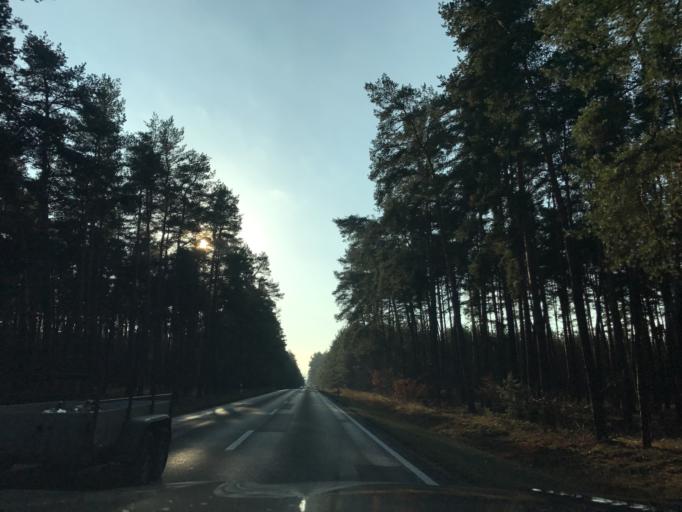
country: DE
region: Brandenburg
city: Wenzlow
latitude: 52.3240
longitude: 12.4854
